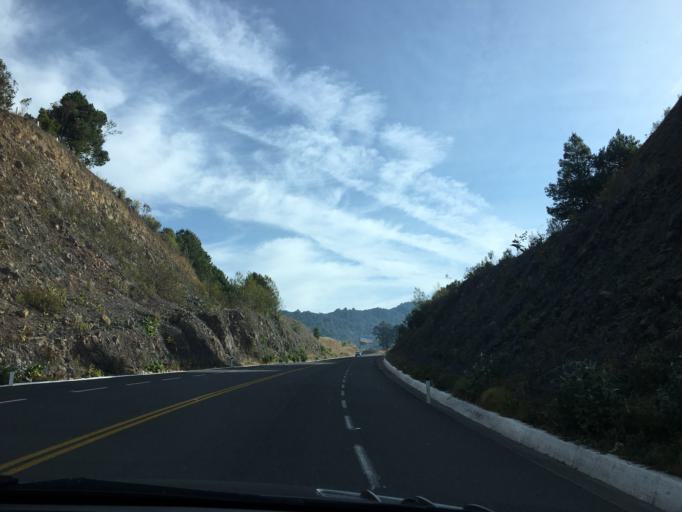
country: MX
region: Mexico
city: San Bartolo
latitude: 19.2703
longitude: -100.0607
